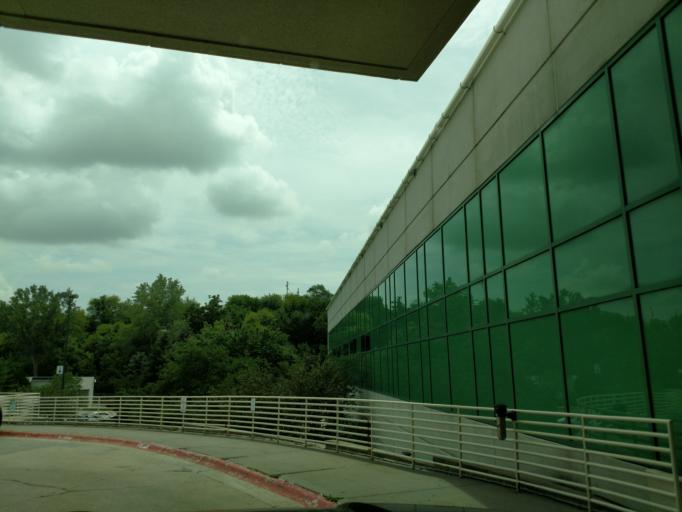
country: US
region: Nebraska
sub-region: Douglas County
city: Omaha
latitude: 41.2512
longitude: -95.9144
